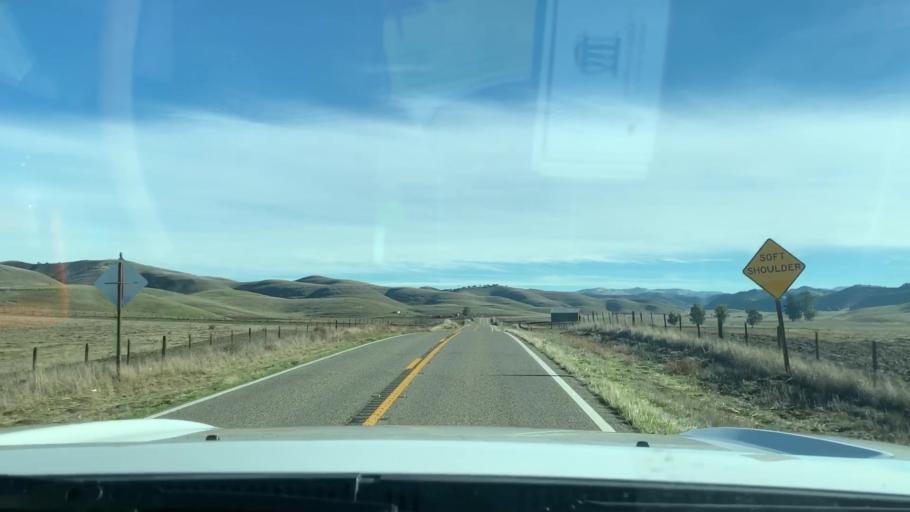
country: US
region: California
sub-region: Monterey County
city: King City
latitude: 36.1638
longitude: -120.8918
